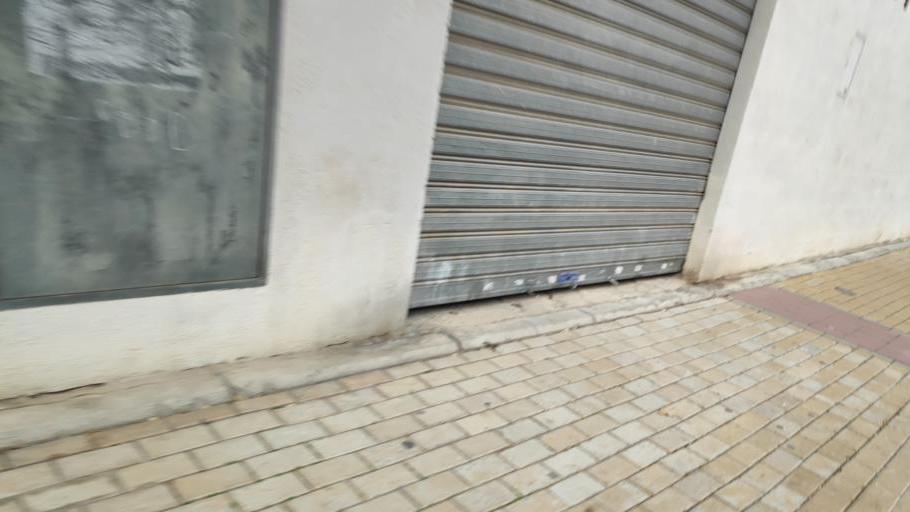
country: ES
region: Valencia
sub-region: Provincia de Castello
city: Castello de la Plana
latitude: 39.9913
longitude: -0.0627
